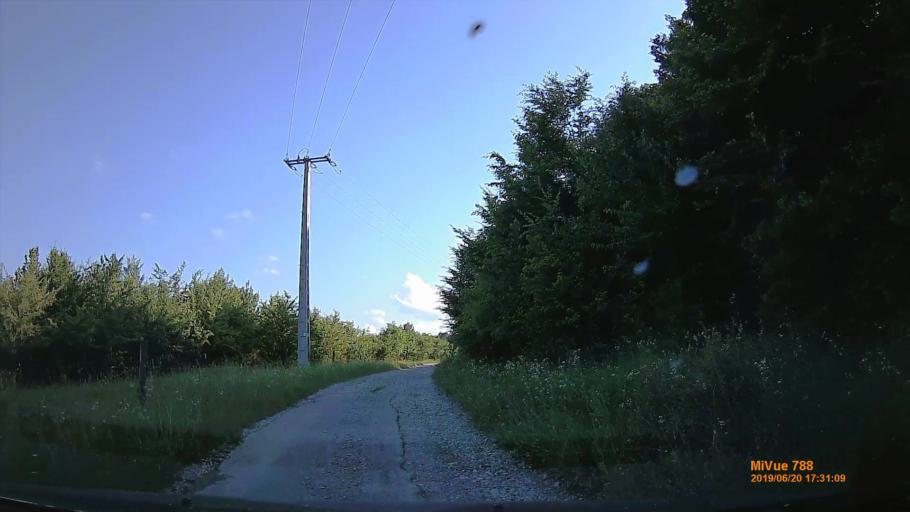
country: HU
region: Baranya
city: Buekkoesd
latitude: 46.1530
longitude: 18.0109
